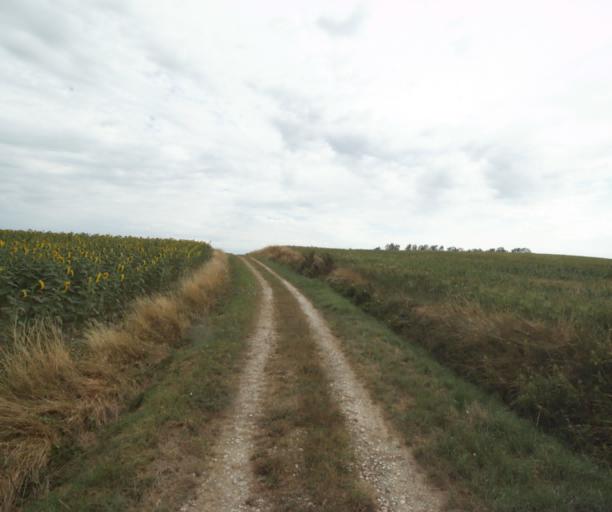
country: FR
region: Midi-Pyrenees
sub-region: Departement de la Haute-Garonne
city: Revel
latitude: 43.4311
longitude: 1.9579
